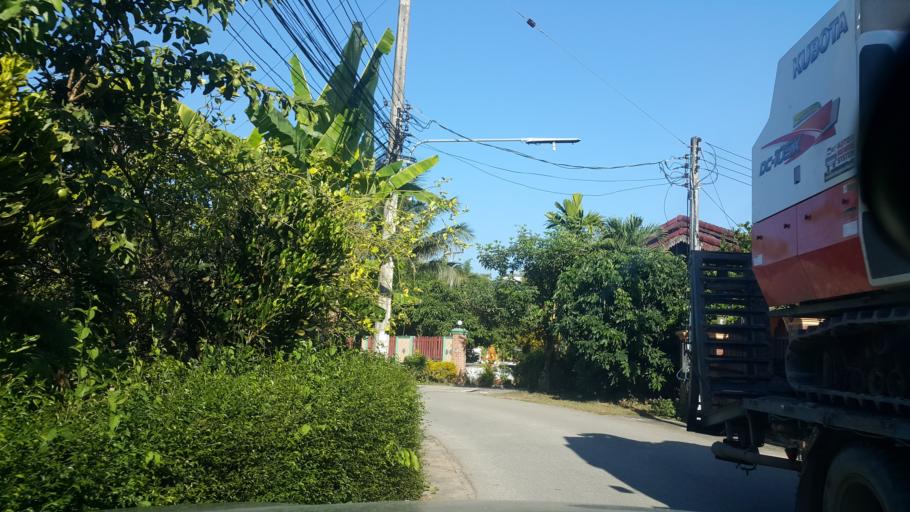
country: TH
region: Chiang Mai
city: Mae On
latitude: 18.7370
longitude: 99.2172
